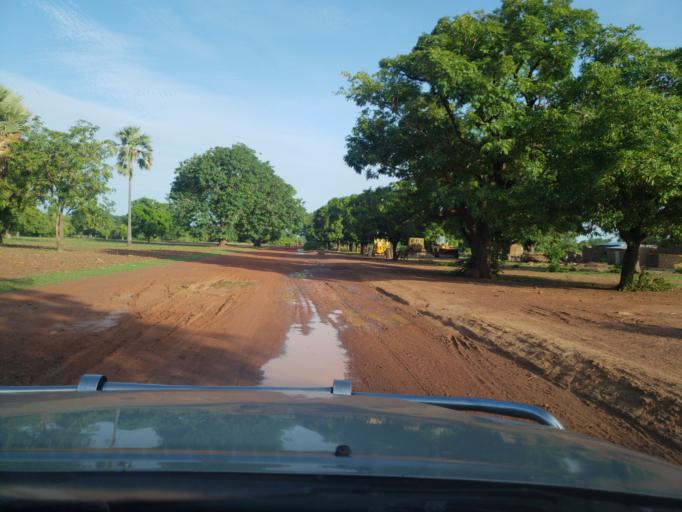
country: ML
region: Sikasso
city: Koutiala
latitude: 12.4212
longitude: -5.5840
